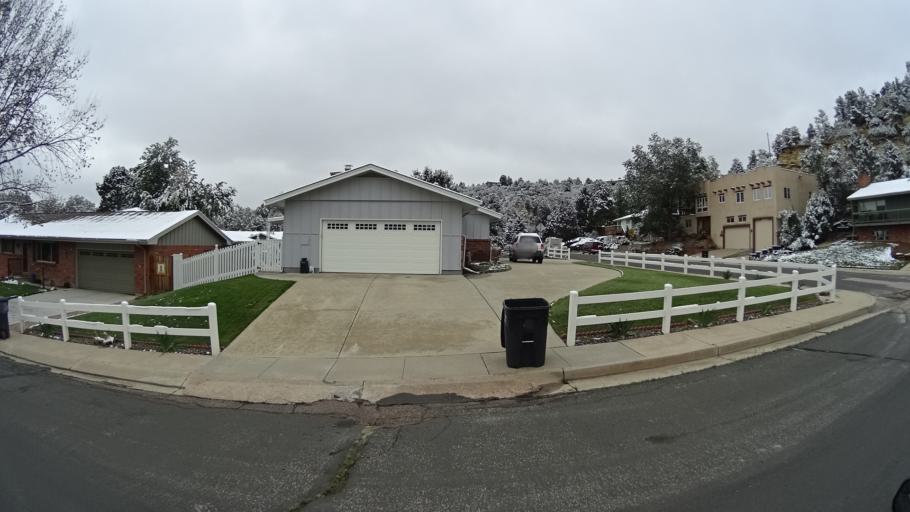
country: US
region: Colorado
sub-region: El Paso County
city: Colorado Springs
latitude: 38.8917
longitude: -104.7772
